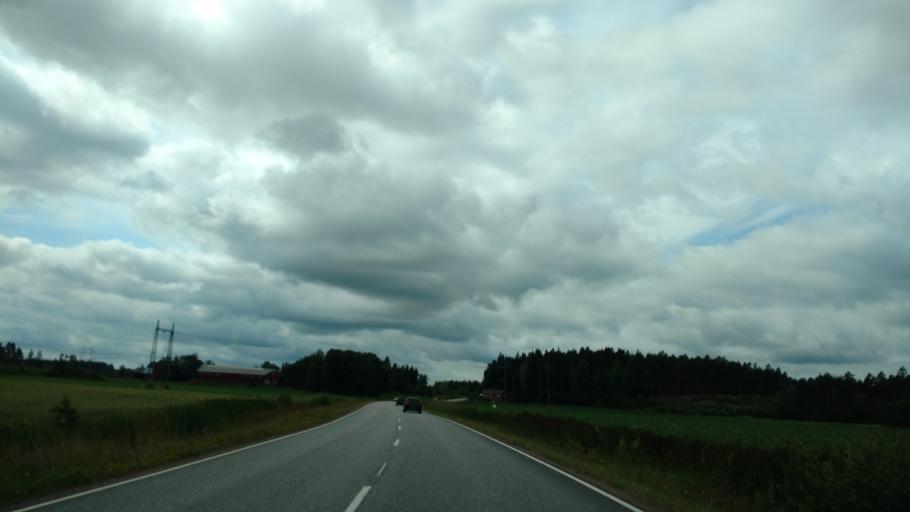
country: FI
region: Varsinais-Suomi
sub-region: Aboland-Turunmaa
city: Kimito
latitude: 60.1375
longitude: 22.6629
